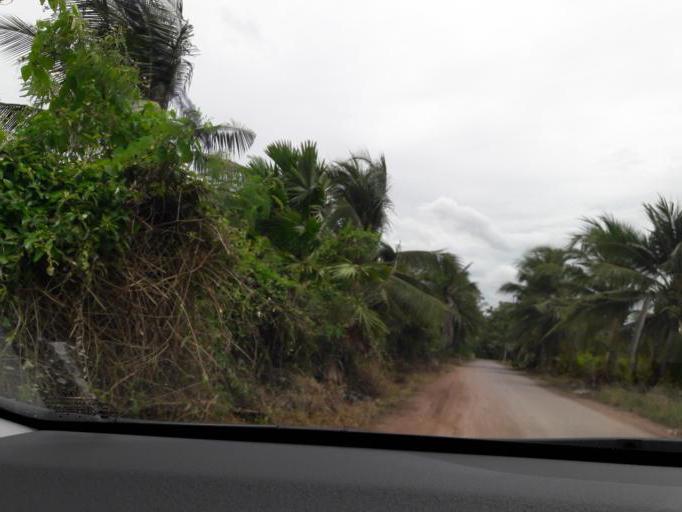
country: TH
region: Samut Sakhon
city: Ban Phaeo
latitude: 13.5499
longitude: 100.0417
